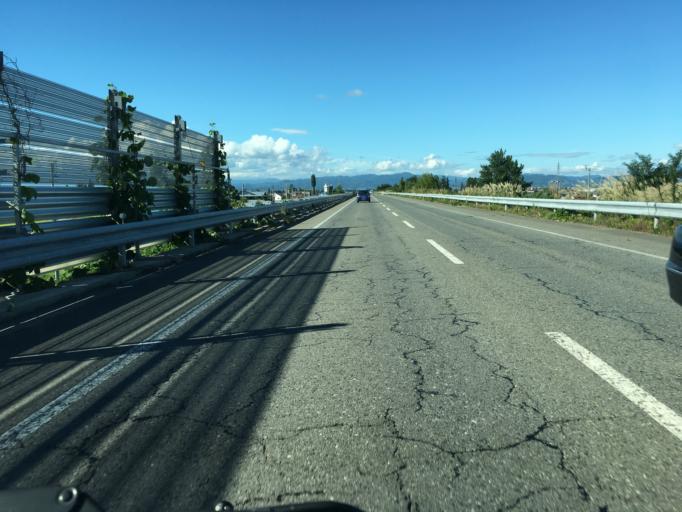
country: JP
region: Yamagata
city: Yonezawa
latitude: 37.9412
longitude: 140.1115
